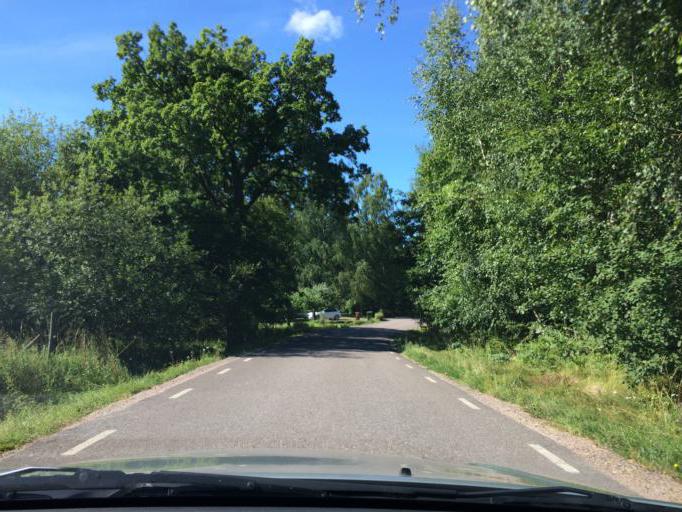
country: SE
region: Soedermanland
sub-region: Eskilstuna Kommun
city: Torshalla
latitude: 59.5084
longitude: 16.4195
